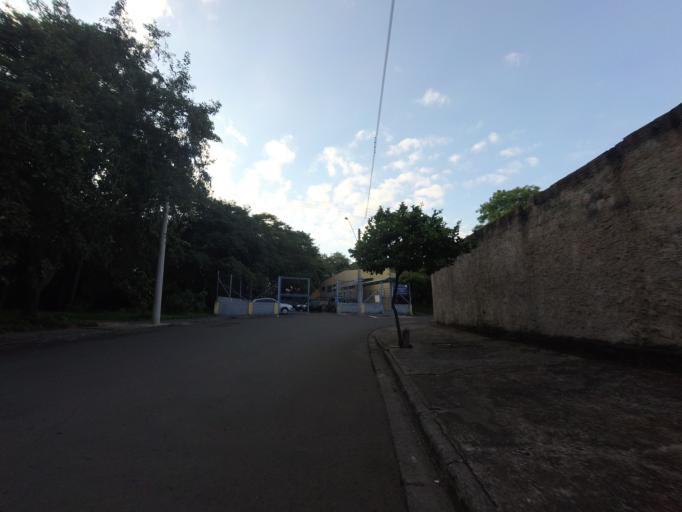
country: BR
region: Sao Paulo
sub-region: Piracicaba
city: Piracicaba
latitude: -22.7587
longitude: -47.6102
